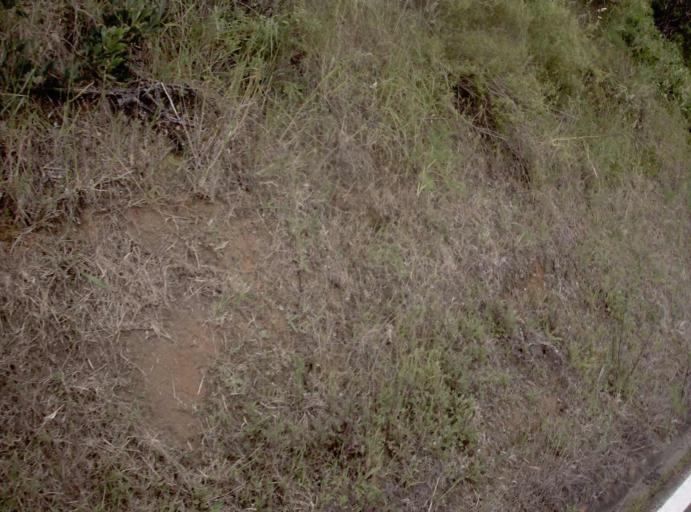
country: AU
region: Victoria
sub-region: East Gippsland
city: Lakes Entrance
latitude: -37.8811
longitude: 147.9658
